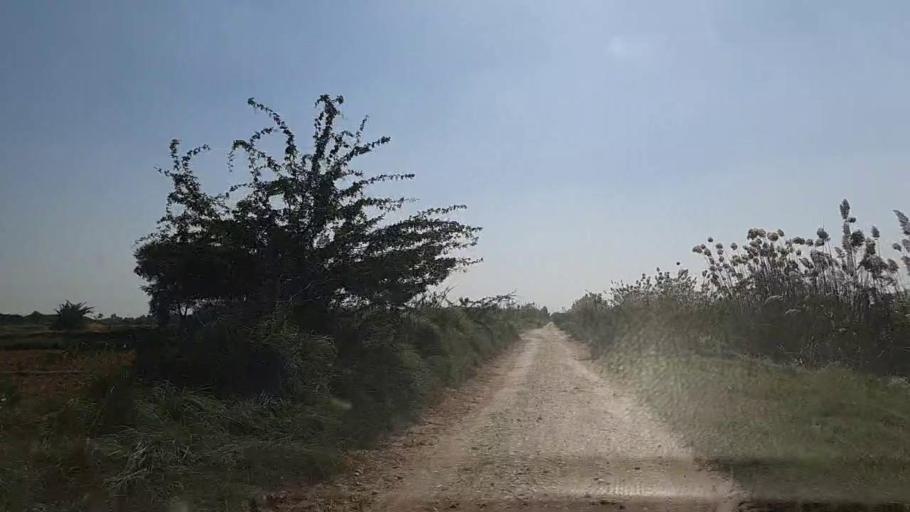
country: PK
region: Sindh
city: Daro Mehar
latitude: 24.8242
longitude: 68.0870
